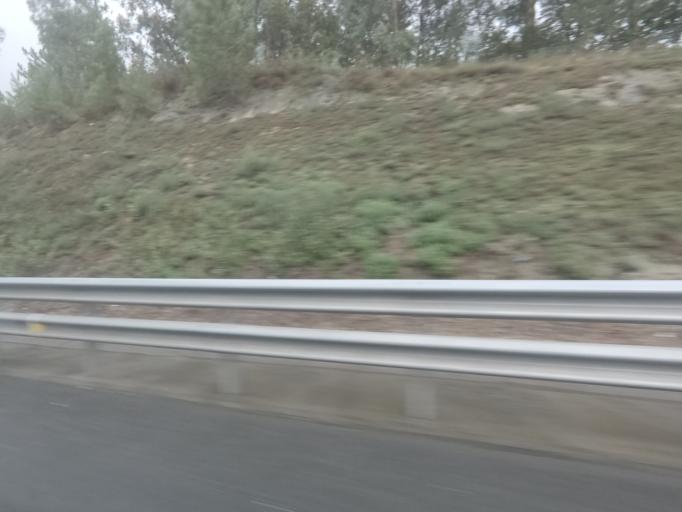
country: ES
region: Galicia
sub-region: Provincia de Pontevedra
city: Vigo
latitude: 42.2340
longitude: -8.6799
